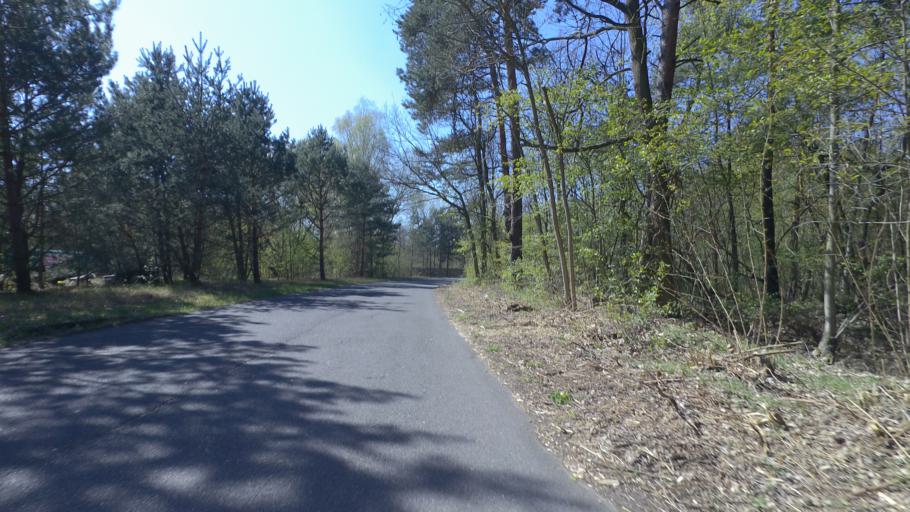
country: DE
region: Brandenburg
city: Zossen
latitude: 52.1665
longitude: 13.4885
